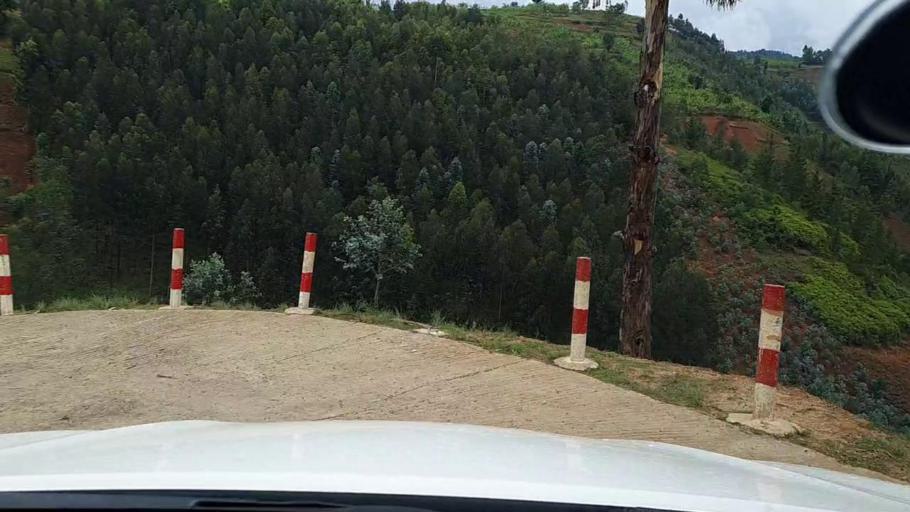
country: RW
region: Western Province
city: Kibuye
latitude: -2.1267
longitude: 29.4279
